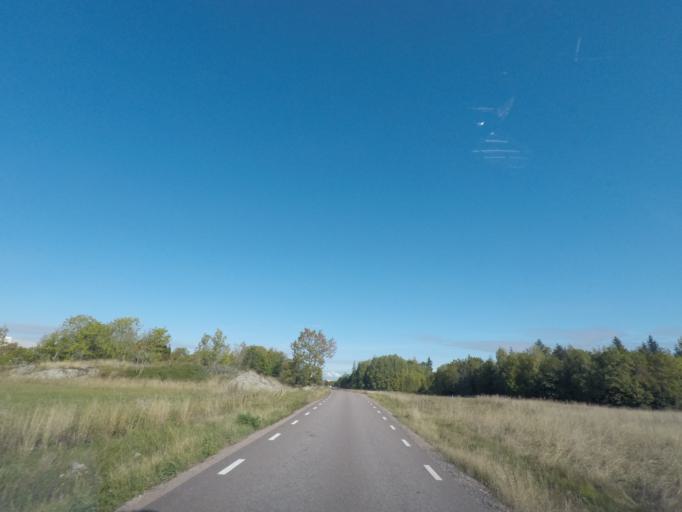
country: SE
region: Vaestmanland
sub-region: Vasteras
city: Vasteras
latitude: 59.5839
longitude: 16.4794
